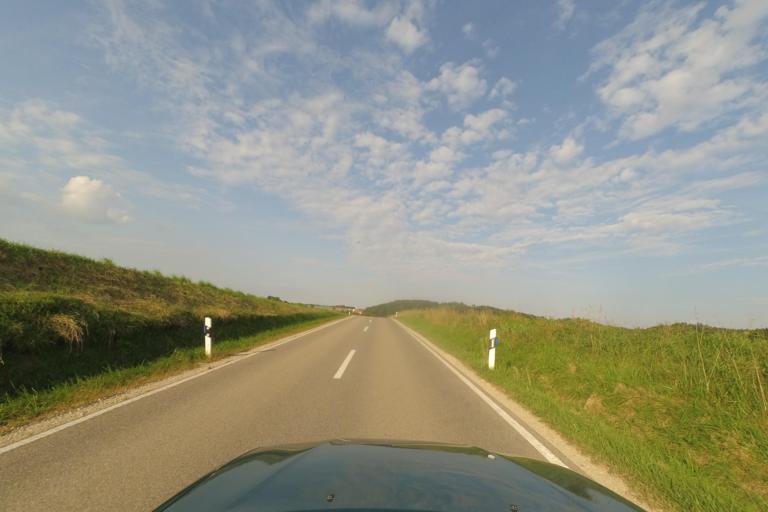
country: DE
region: Bavaria
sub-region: Upper Bavaria
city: Nandlstadt
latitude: 48.5896
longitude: 11.8222
